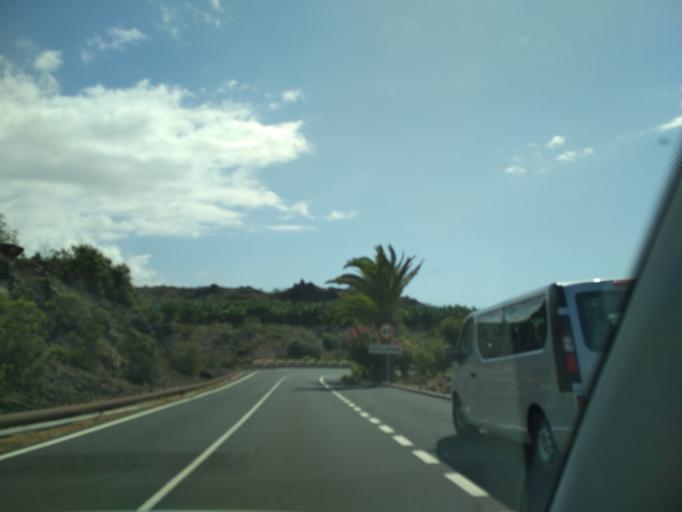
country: ES
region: Canary Islands
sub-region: Provincia de Santa Cruz de Tenerife
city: Santiago del Teide
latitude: 28.2394
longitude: -16.8370
